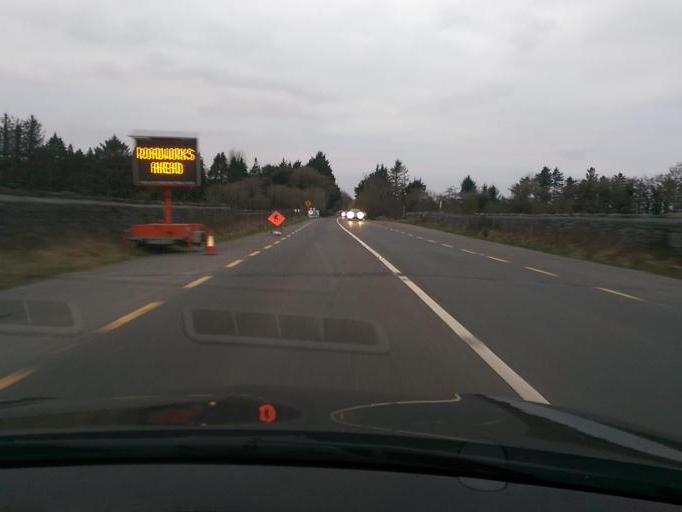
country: IE
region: Connaught
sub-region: County Galway
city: Moycullen
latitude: 53.3204
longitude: -9.1588
